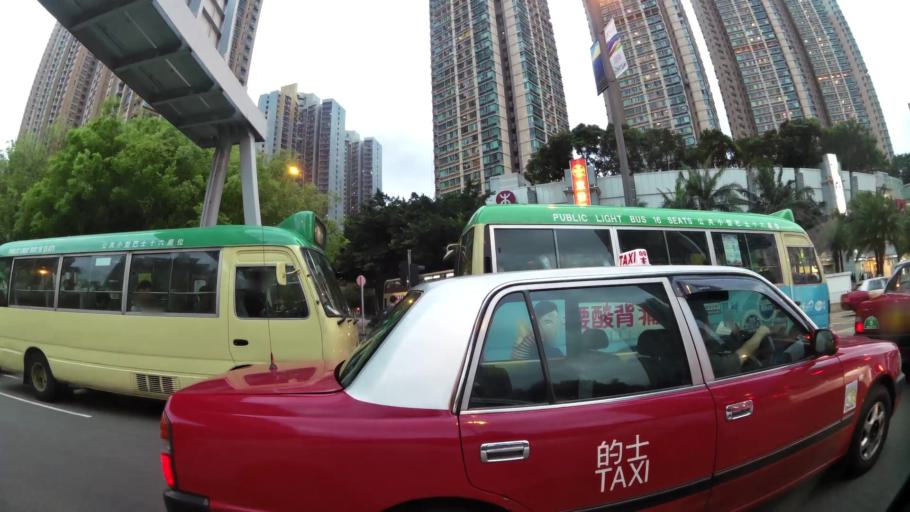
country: HK
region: Sham Shui Po
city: Sham Shui Po
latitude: 22.3182
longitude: 114.1628
